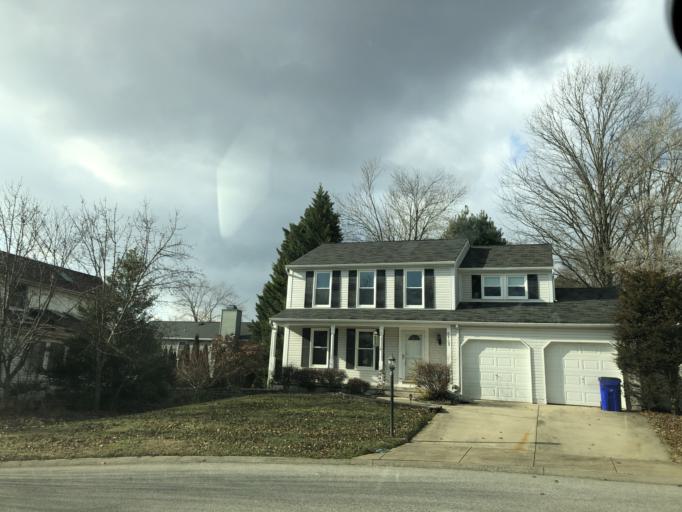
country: US
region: Maryland
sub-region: Howard County
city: Columbia
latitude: 39.1959
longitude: -76.8280
